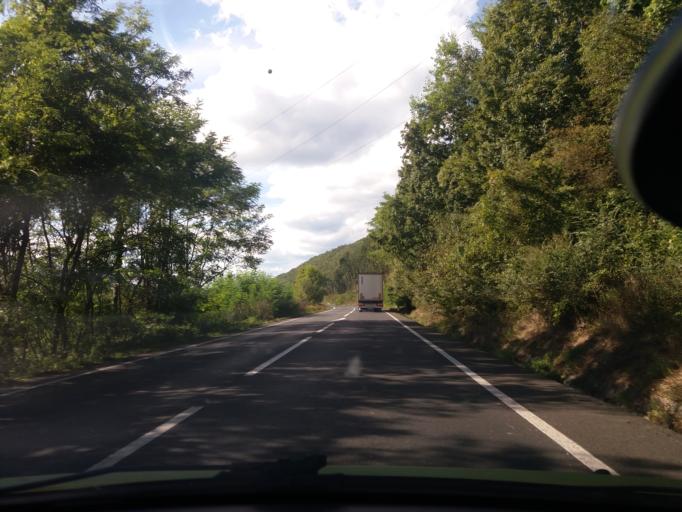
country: RO
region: Hunedoara
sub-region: Comuna Zam
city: Zam
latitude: 46.0139
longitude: 22.4256
